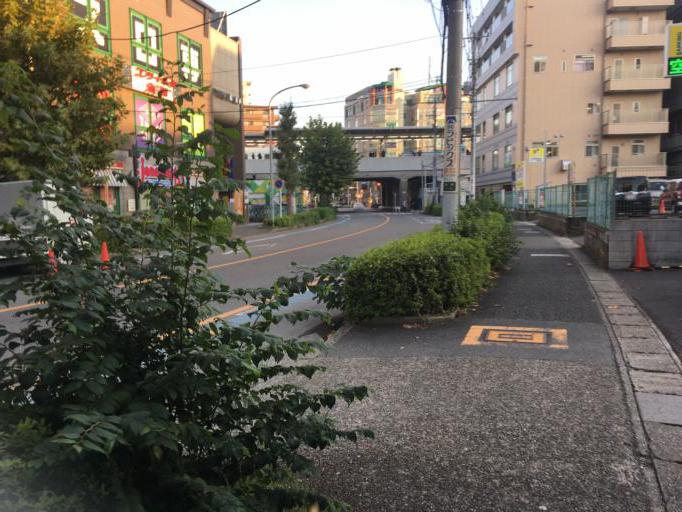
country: JP
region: Saitama
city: Shiki
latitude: 35.8164
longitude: 139.5870
